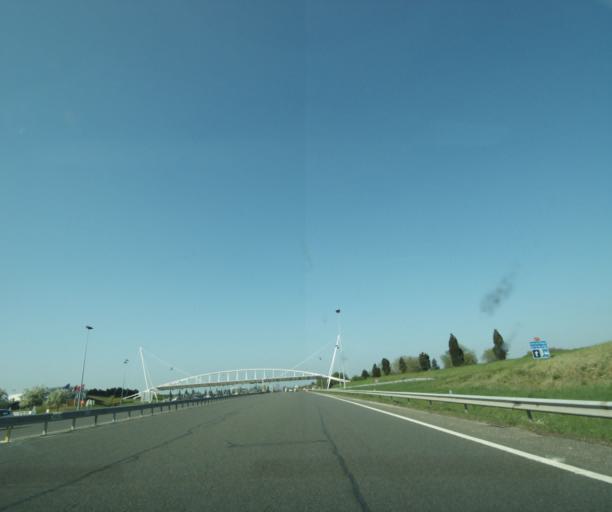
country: FR
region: Centre
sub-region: Departement du Loiret
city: Dordives
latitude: 48.1744
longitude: 2.7671
